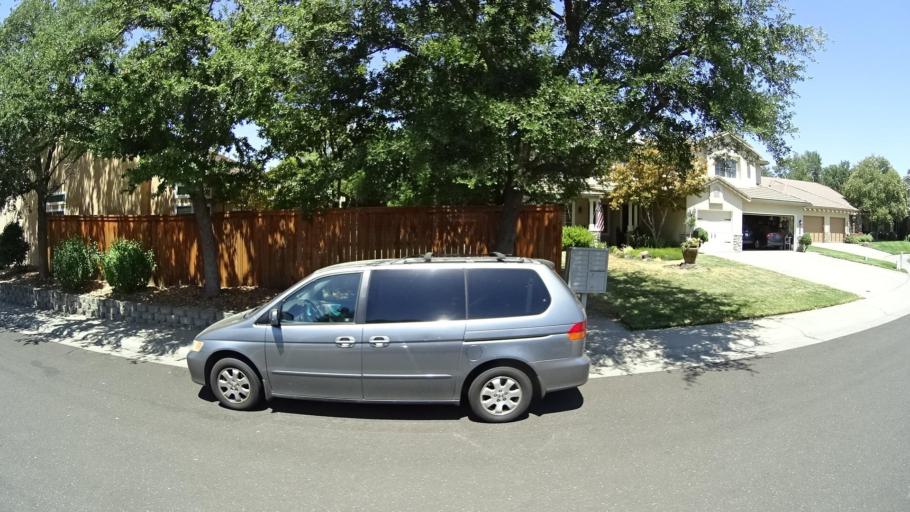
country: US
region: California
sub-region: Placer County
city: Rocklin
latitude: 38.8277
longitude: -121.2551
